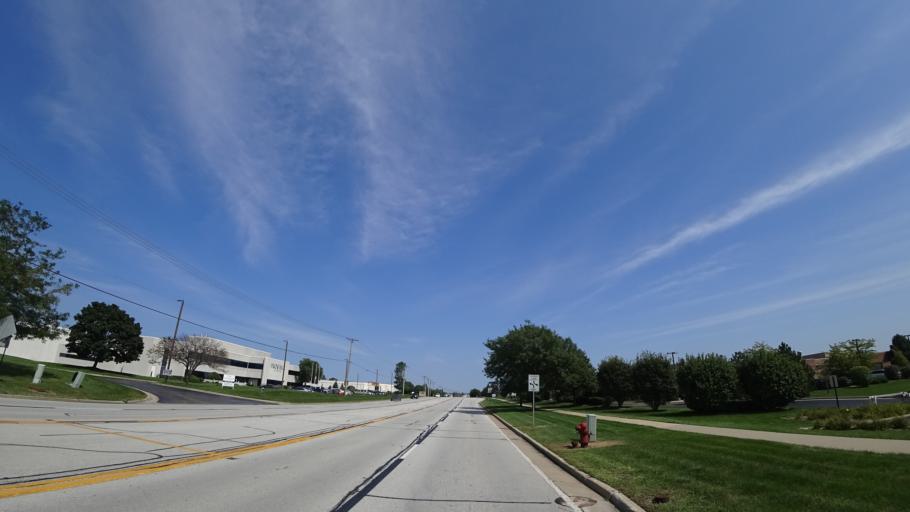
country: US
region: Illinois
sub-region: Cook County
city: Orland Hills
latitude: 41.5432
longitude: -87.8412
